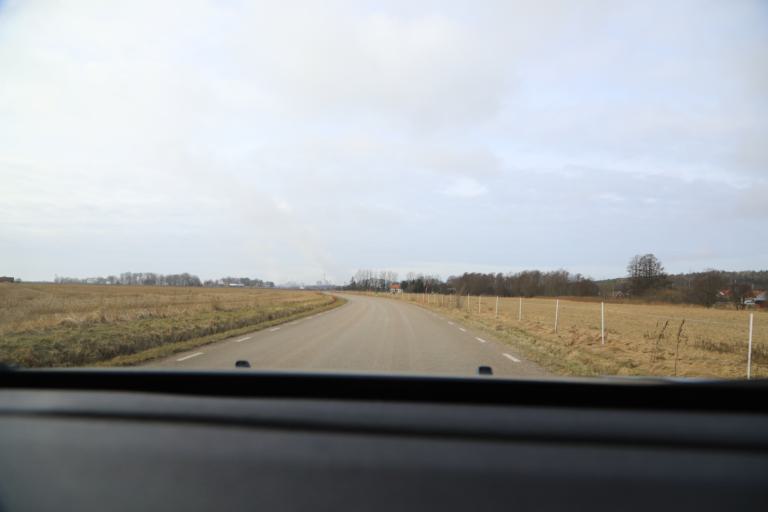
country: SE
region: Halland
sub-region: Varbergs Kommun
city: Veddige
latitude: 57.2289
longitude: 12.2383
